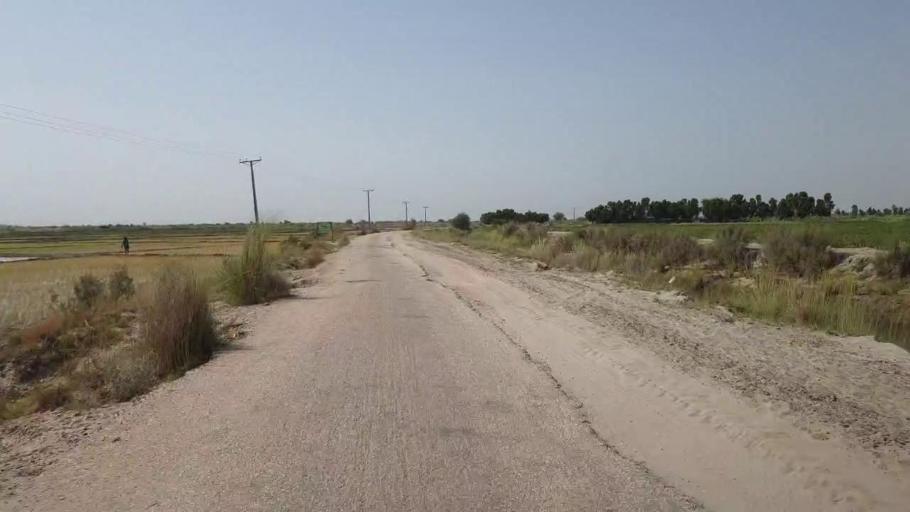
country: PK
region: Sindh
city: Jam Sahib
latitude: 26.4183
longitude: 68.9081
